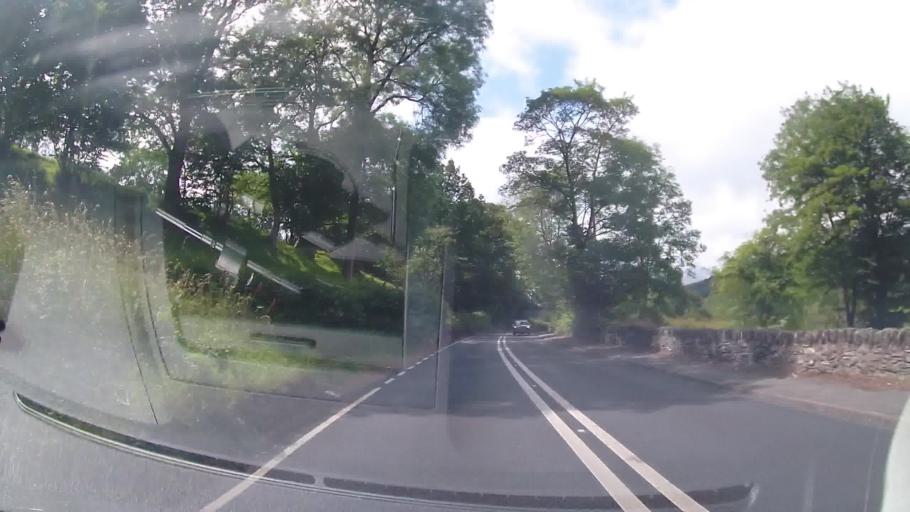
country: GB
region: Wales
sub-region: Denbighshire
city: Corwen
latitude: 52.9765
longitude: -3.3297
